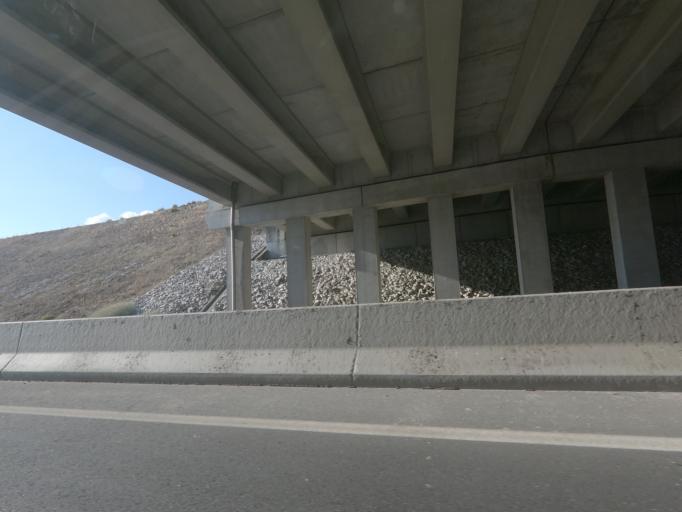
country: PT
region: Vila Real
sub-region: Chaves
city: Chaves
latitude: 41.8048
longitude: -7.4139
